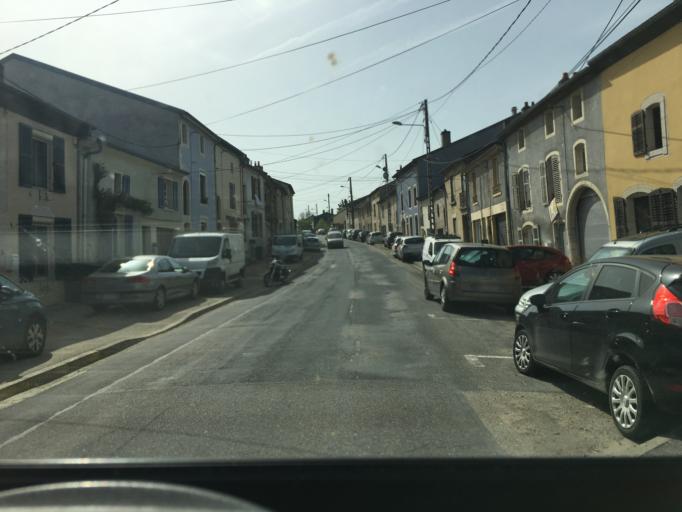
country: FR
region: Lorraine
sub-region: Departement de Meurthe-et-Moselle
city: Chaligny
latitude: 48.6349
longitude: 6.0465
